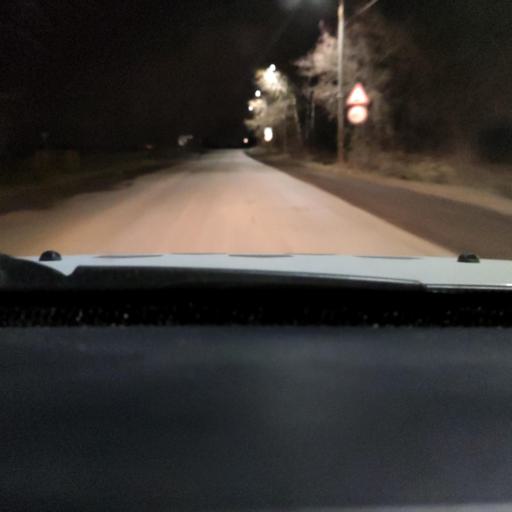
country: RU
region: Perm
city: Gamovo
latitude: 57.8742
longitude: 56.1020
